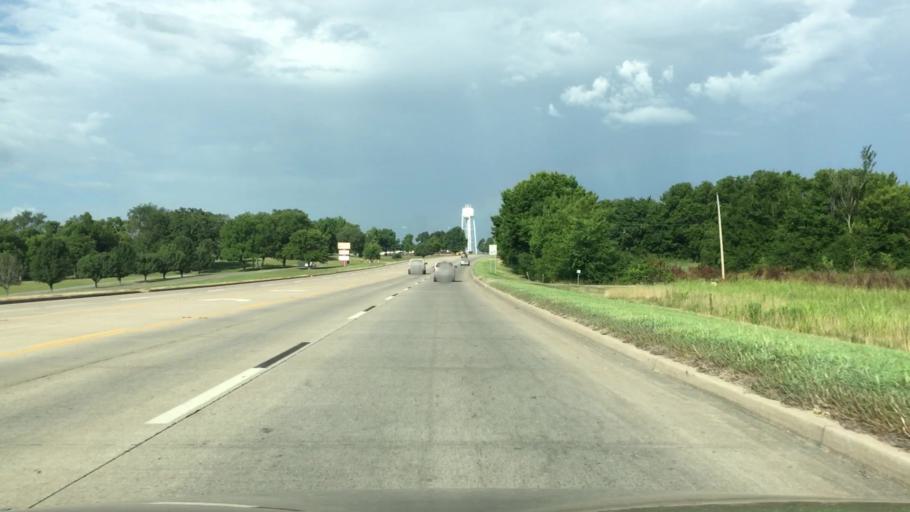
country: US
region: Oklahoma
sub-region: Cherokee County
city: Park Hill
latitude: 35.8522
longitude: -94.9939
